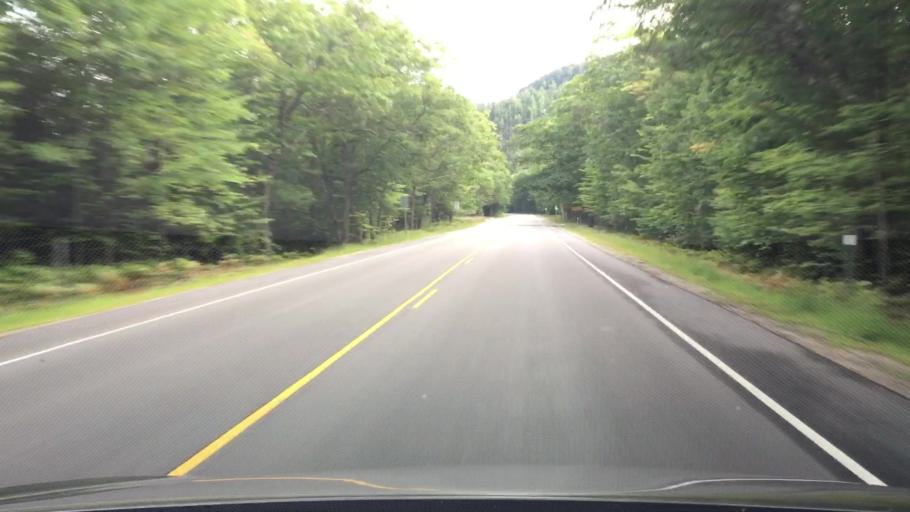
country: US
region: New Hampshire
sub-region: Carroll County
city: North Conway
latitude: 44.0079
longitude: -71.2433
